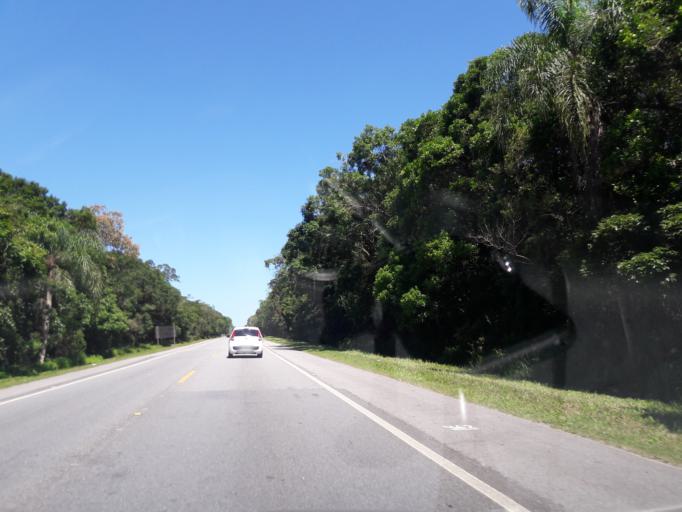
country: BR
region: Parana
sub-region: Pontal Do Parana
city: Pontal do Parana
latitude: -25.6337
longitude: -48.5375
